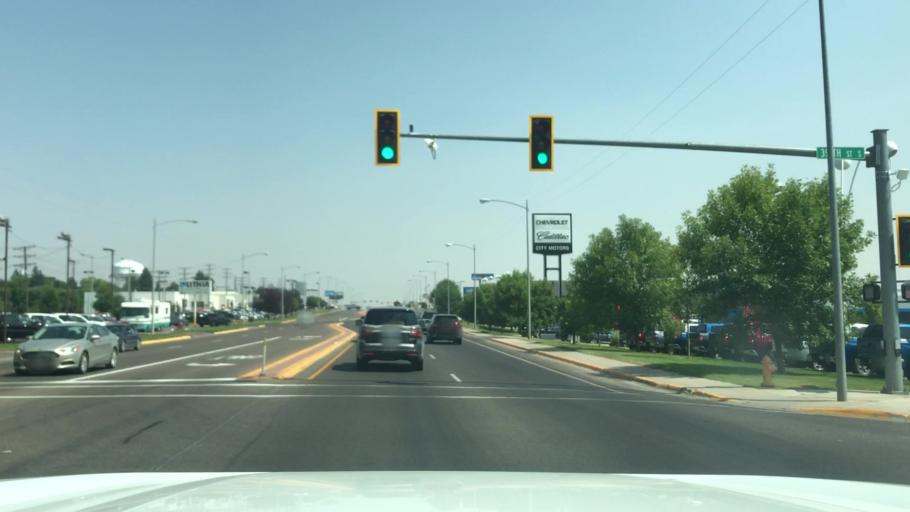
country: US
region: Montana
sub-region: Cascade County
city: Malmstrom Air Force Base
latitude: 47.4939
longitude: -111.2400
